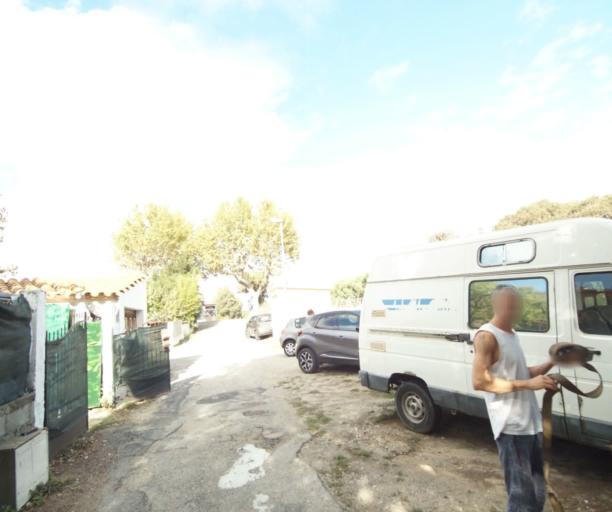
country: FR
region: Languedoc-Roussillon
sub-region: Departement des Pyrenees-Orientales
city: Argelers
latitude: 42.5448
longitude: 3.0151
